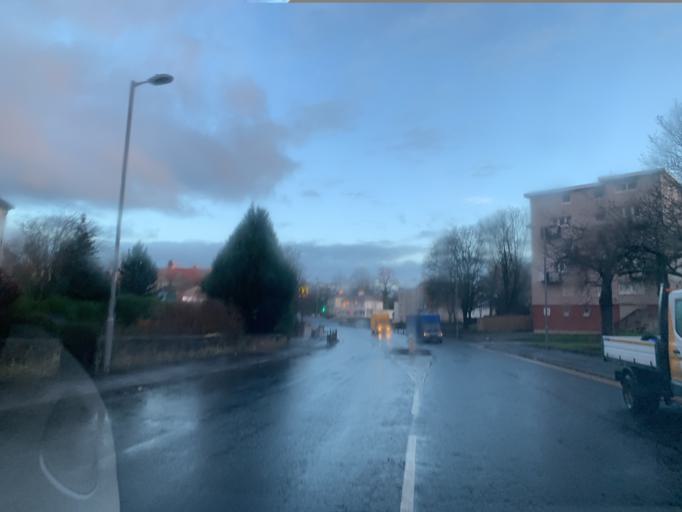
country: GB
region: Scotland
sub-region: East Renfrewshire
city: Giffnock
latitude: 55.8080
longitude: -4.3154
